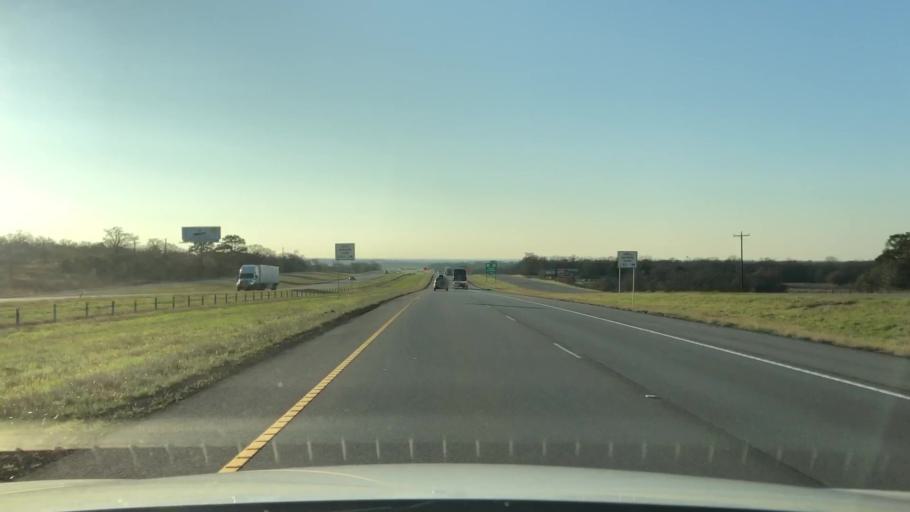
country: US
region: Texas
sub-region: Caldwell County
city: Luling
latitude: 29.6541
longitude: -97.5665
